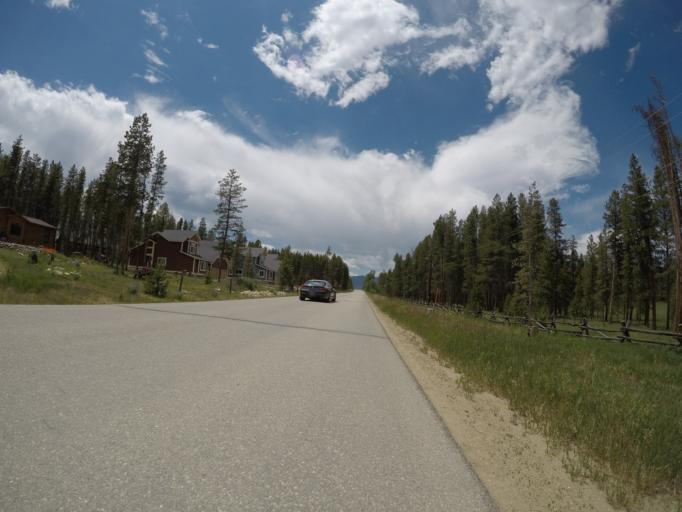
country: US
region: Colorado
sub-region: Grand County
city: Fraser
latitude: 39.9520
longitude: -105.7947
